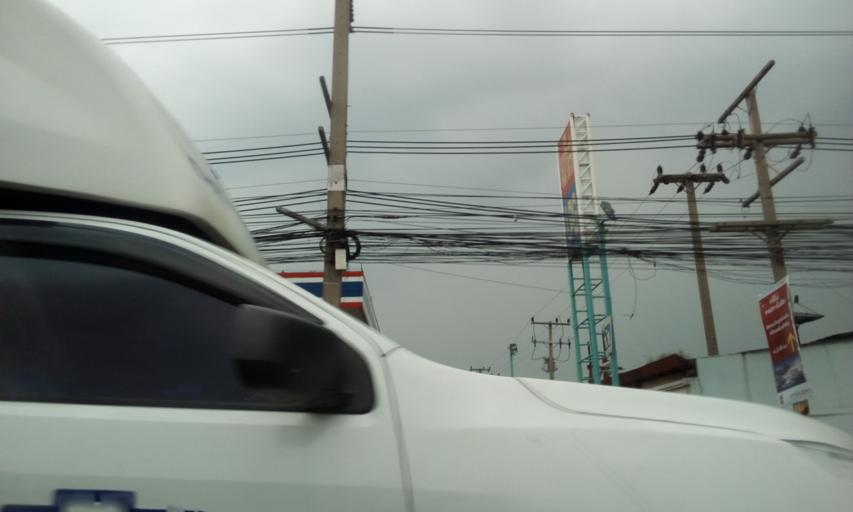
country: TH
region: Phra Nakhon Si Ayutthaya
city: Ban Bang Kadi Pathum Thani
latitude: 13.9852
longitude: 100.5945
